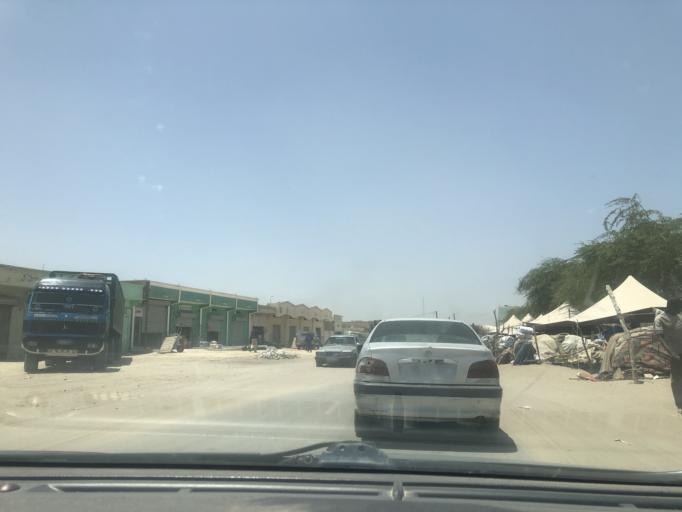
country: MR
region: Nouakchott
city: Nouakchott
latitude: 18.0754
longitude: -15.9833
